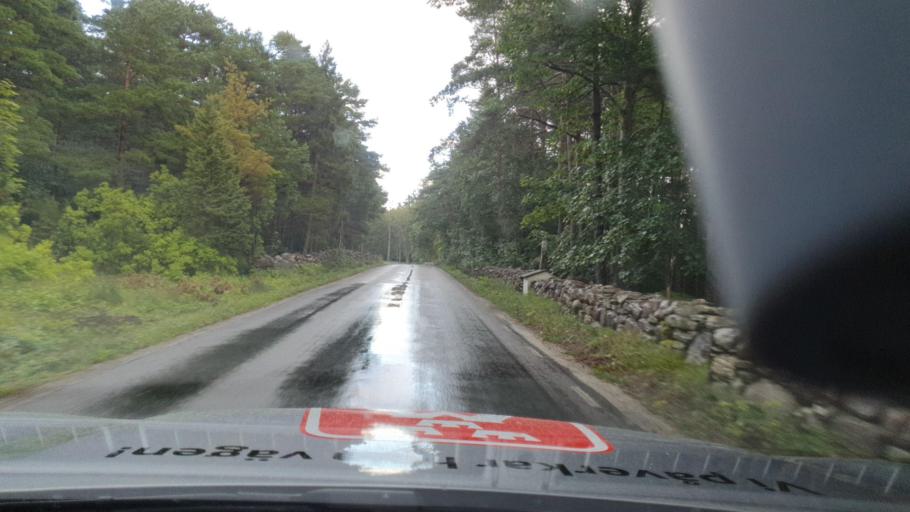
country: SE
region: Gotland
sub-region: Gotland
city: Vibble
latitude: 57.5318
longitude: 18.2420
